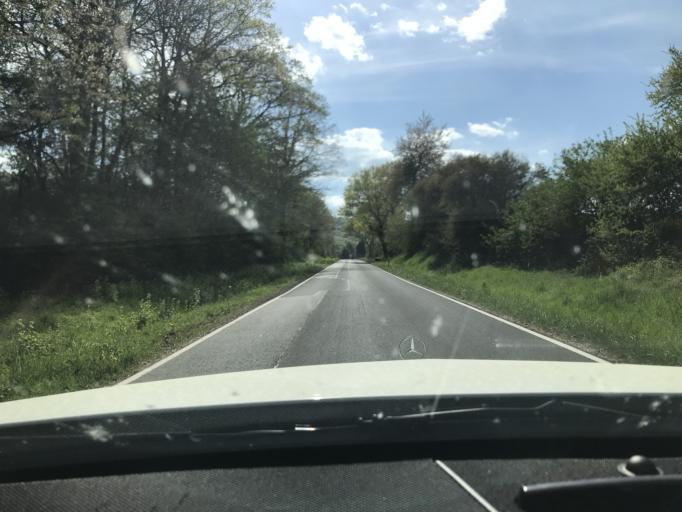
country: DE
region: Hesse
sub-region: Regierungsbezirk Kassel
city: Weissenborn
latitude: 51.1272
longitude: 10.1281
